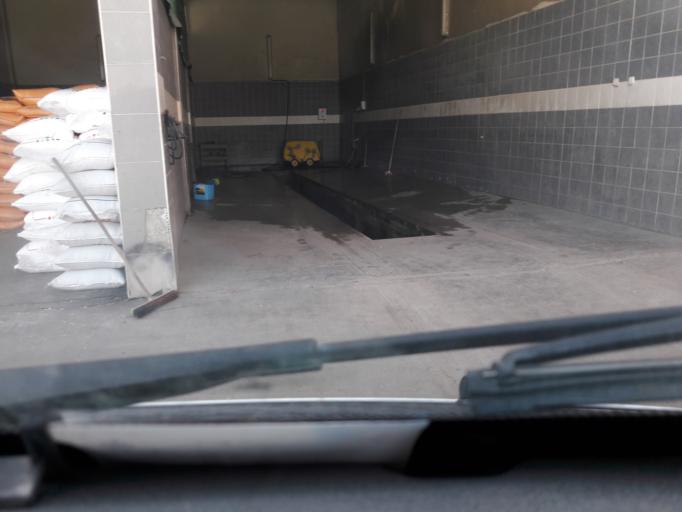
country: TR
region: Gumushane
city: Kelkit
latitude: 40.1417
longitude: 39.4330
